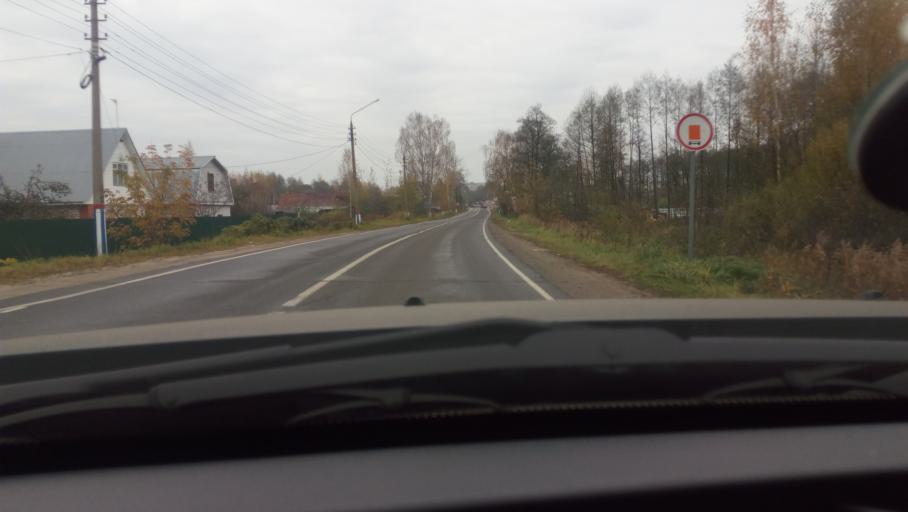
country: RU
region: Moskovskaya
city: Likino-Dulevo
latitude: 55.7014
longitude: 38.9408
